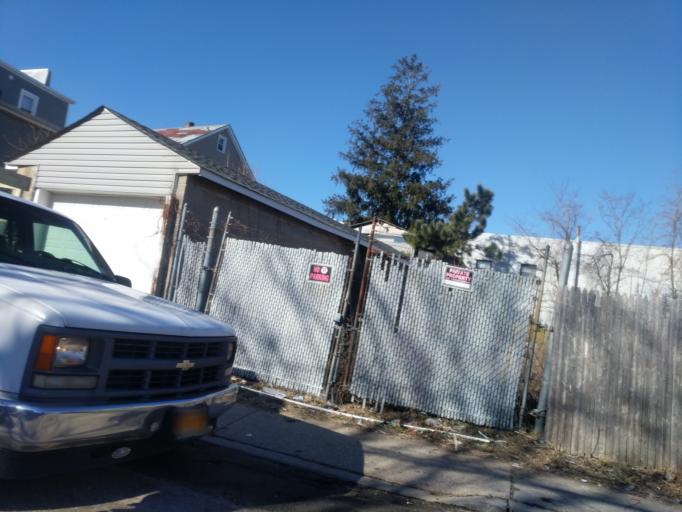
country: US
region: New York
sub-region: Nassau County
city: Inwood
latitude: 40.6190
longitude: -73.7396
